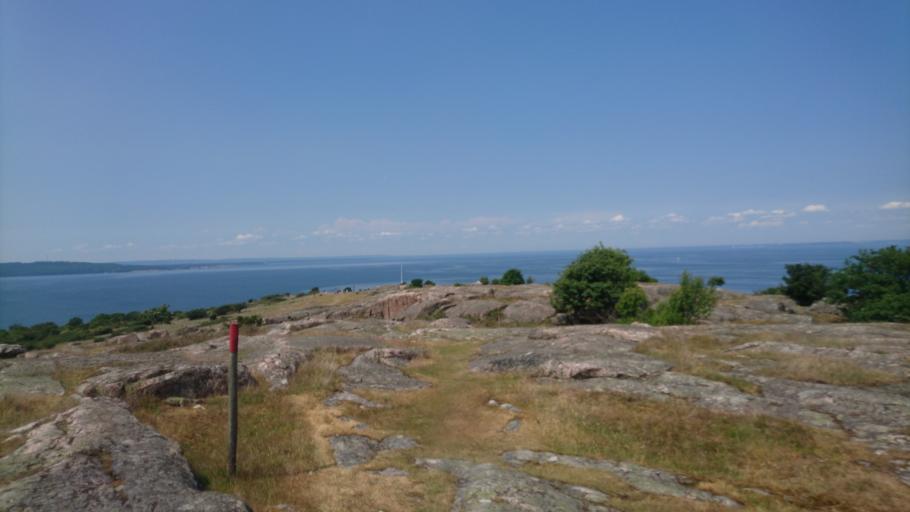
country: SE
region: Blekinge
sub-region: Karlshamns Kommun
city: Karlshamn
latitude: 56.0149
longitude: 14.8410
